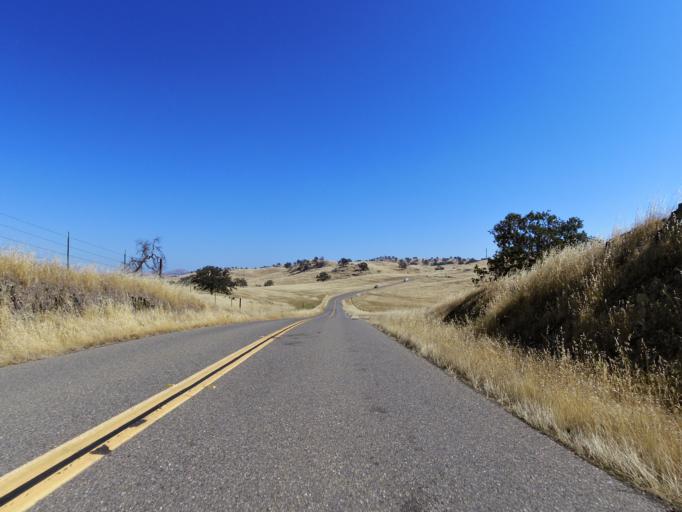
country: US
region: California
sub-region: Merced County
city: Planada
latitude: 37.5423
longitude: -120.3291
